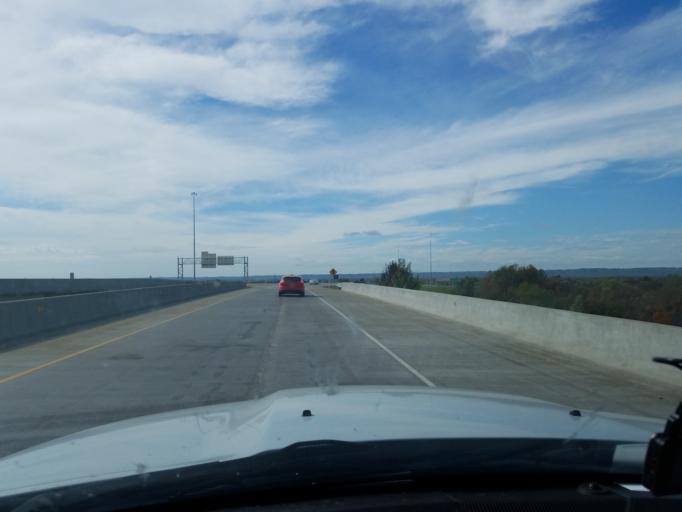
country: US
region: Indiana
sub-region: Clark County
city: Oak Park
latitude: 38.3447
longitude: -85.7099
